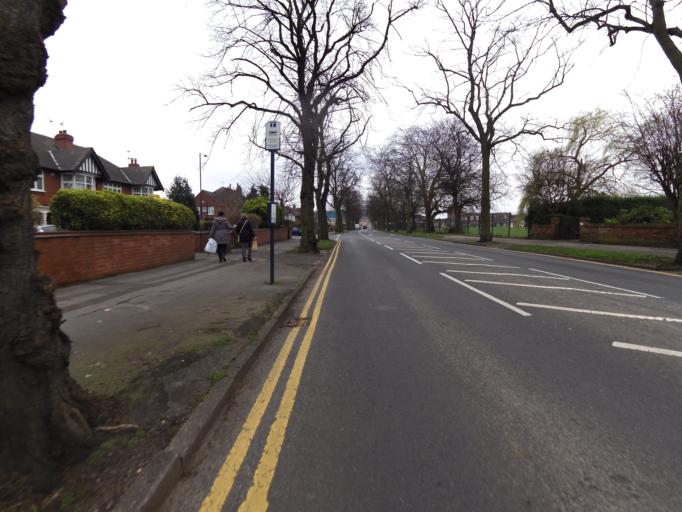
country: GB
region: England
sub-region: Doncaster
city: Doncaster
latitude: 53.5231
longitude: -1.1104
